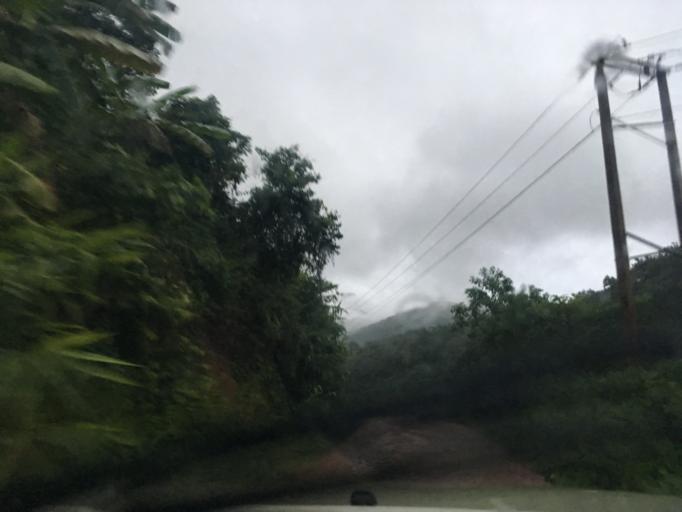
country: LA
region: Oudomxai
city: Muang La
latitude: 21.2470
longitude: 101.9334
